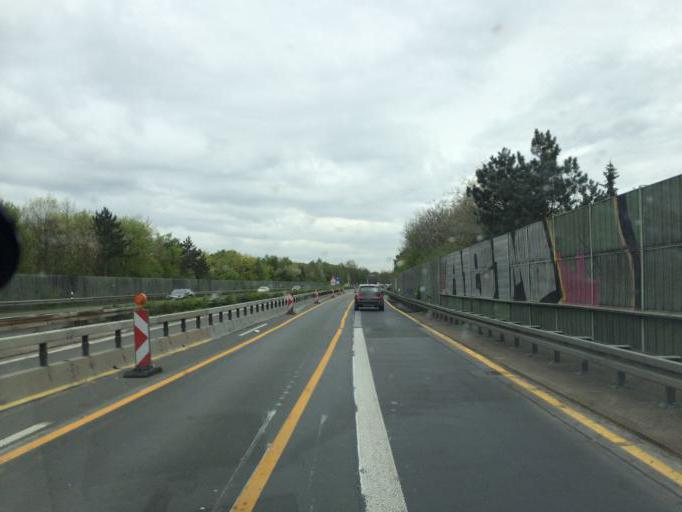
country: DE
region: North Rhine-Westphalia
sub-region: Regierungsbezirk Munster
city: Recklinghausen
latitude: 51.6662
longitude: 7.1571
